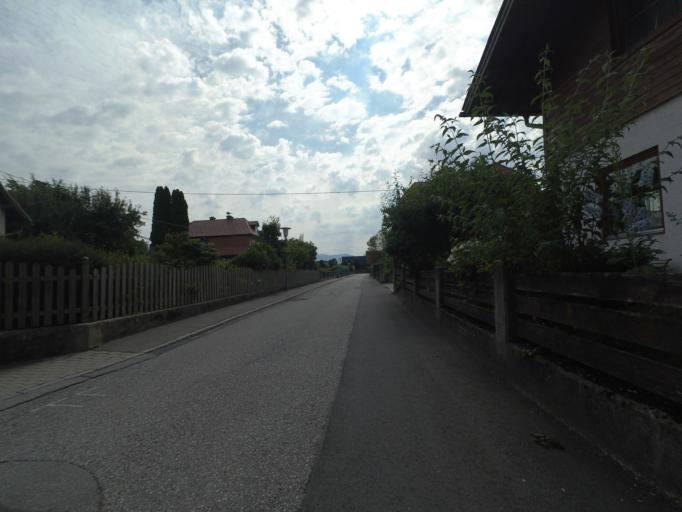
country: DE
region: Bavaria
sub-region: Upper Bavaria
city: Freilassing
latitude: 47.8112
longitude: 12.9877
